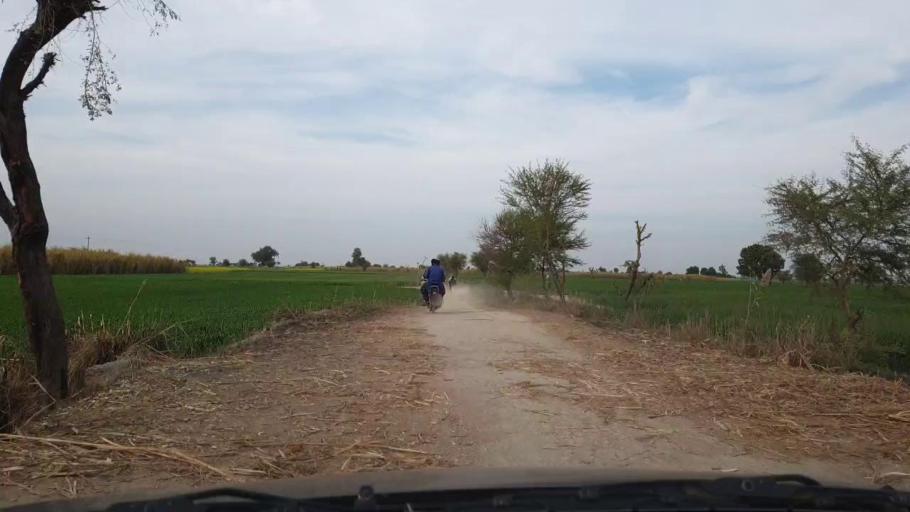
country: PK
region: Sindh
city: Khadro
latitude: 26.1673
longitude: 68.7300
